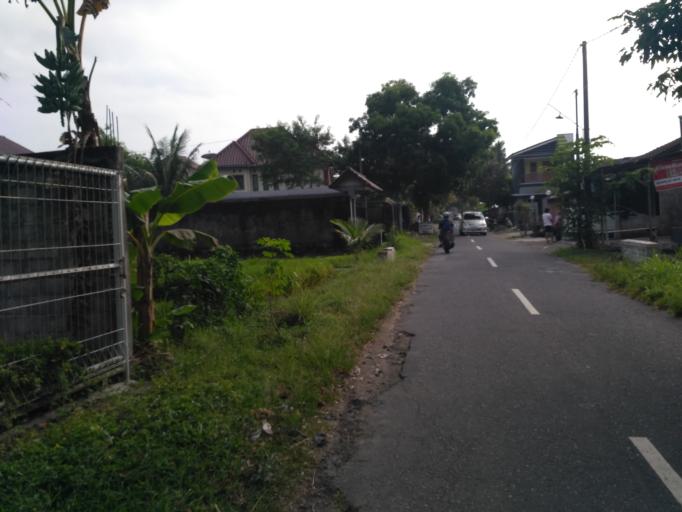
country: ID
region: Daerah Istimewa Yogyakarta
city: Melati
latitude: -7.7180
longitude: 110.3989
